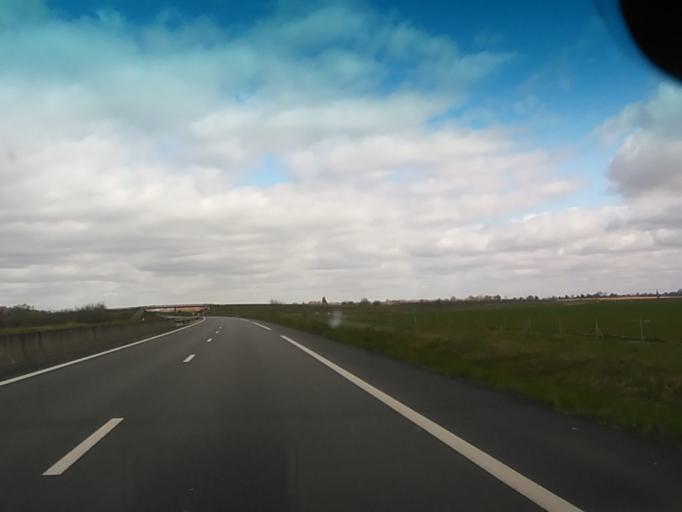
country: FR
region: Haute-Normandie
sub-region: Departement de l'Eure
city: Thiberville
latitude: 49.1172
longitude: 0.5260
